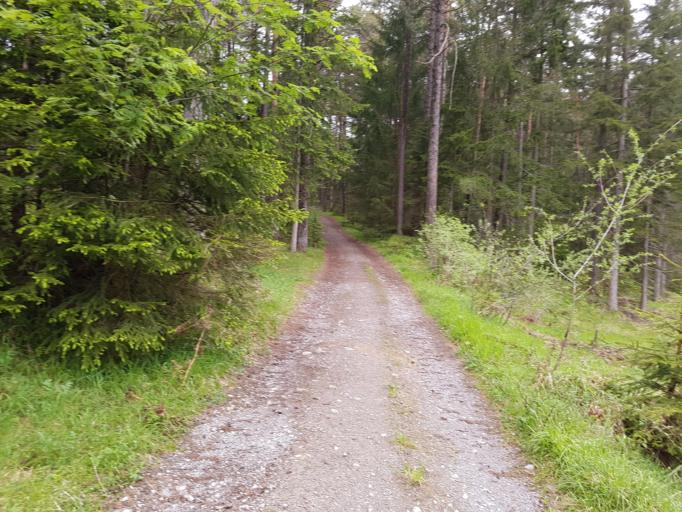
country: AT
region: Tyrol
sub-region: Politischer Bezirk Imst
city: Obsteig
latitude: 47.3017
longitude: 10.9434
